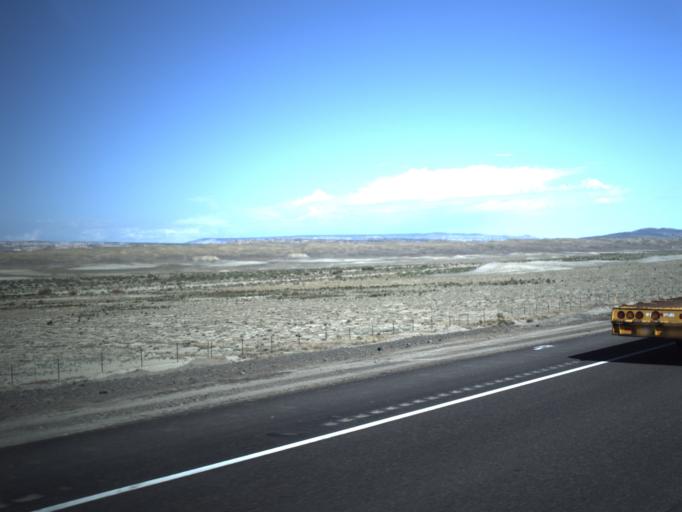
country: US
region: Utah
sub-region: Carbon County
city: East Carbon City
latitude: 39.0366
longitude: -110.3065
